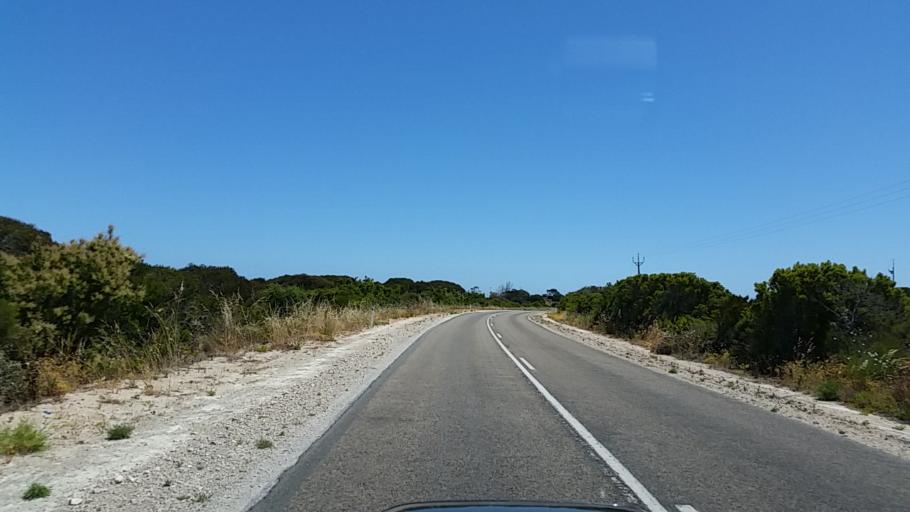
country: AU
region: South Australia
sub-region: Yorke Peninsula
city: Honiton
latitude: -35.2229
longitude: 136.9936
